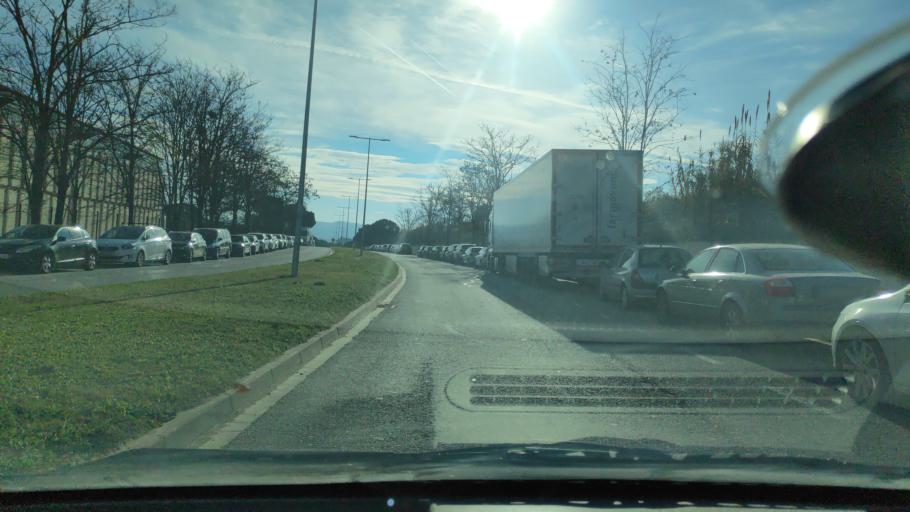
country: ES
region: Catalonia
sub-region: Provincia de Barcelona
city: Rubi
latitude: 41.4905
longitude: 2.0480
